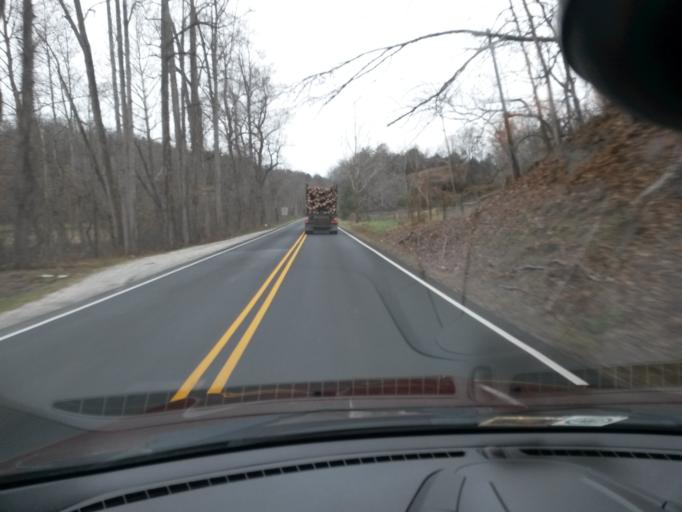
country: US
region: Virginia
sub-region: Amherst County
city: Amherst
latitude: 37.6592
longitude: -79.1500
